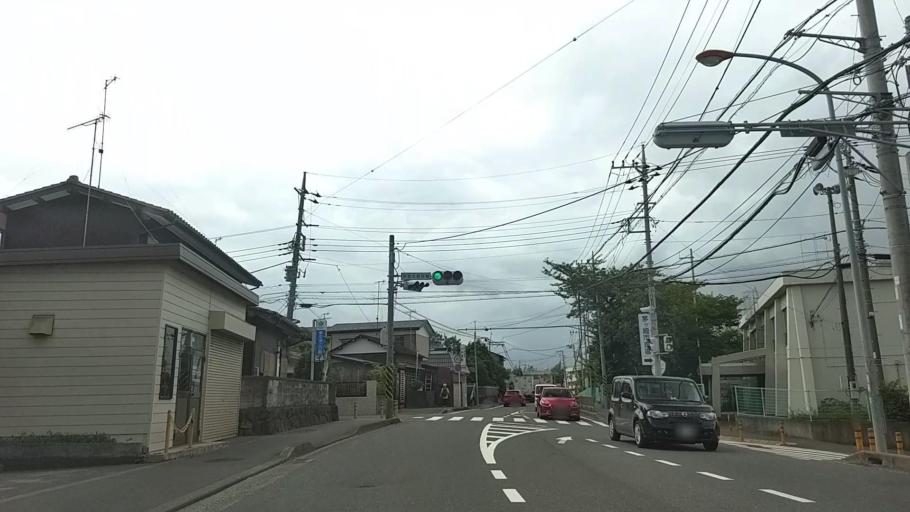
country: JP
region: Kanagawa
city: Chigasaki
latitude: 35.3707
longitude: 139.4245
